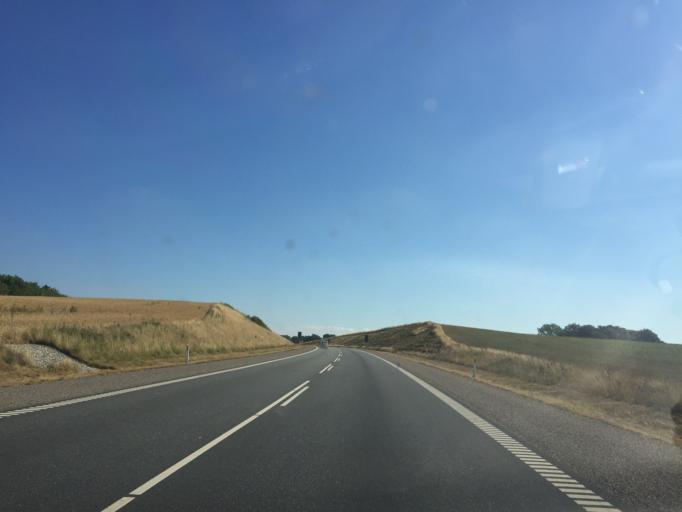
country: DK
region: Capital Region
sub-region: Egedal Kommune
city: Smorumnedre
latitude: 55.7477
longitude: 12.2827
